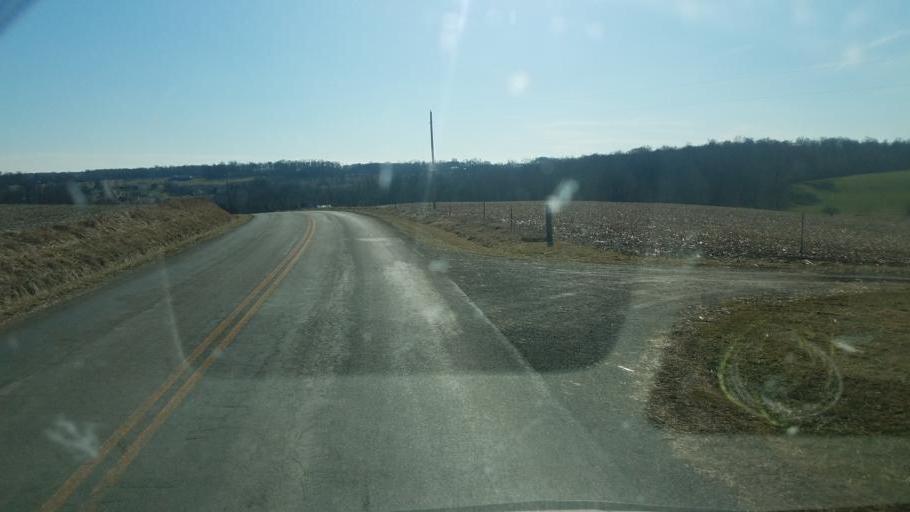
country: US
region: Ohio
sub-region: Knox County
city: Fredericktown
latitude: 40.5063
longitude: -82.4240
